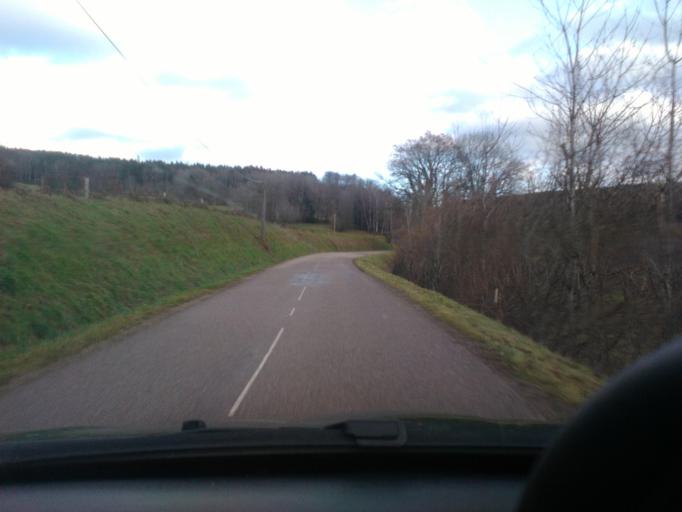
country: FR
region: Lorraine
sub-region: Departement des Vosges
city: Senones
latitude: 48.3363
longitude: 7.0112
